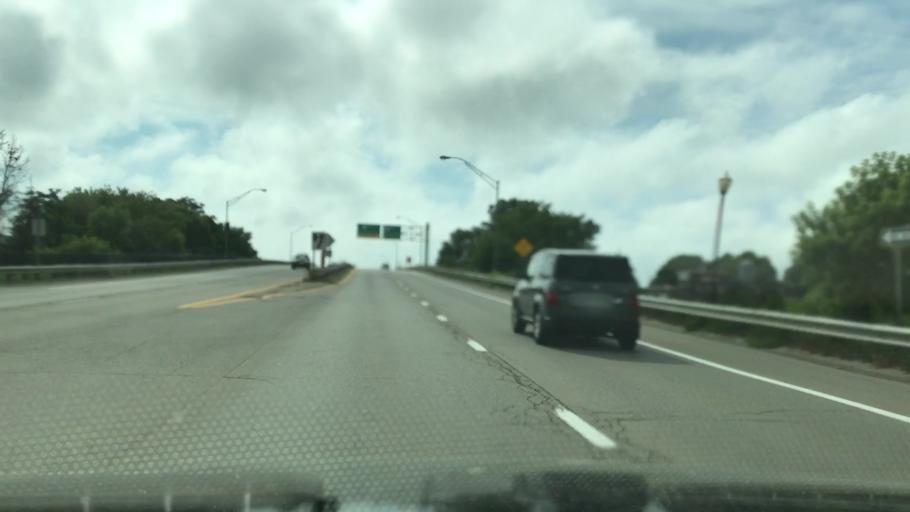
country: US
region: Michigan
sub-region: Ottawa County
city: Ferrysburg
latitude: 43.0763
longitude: -86.2108
